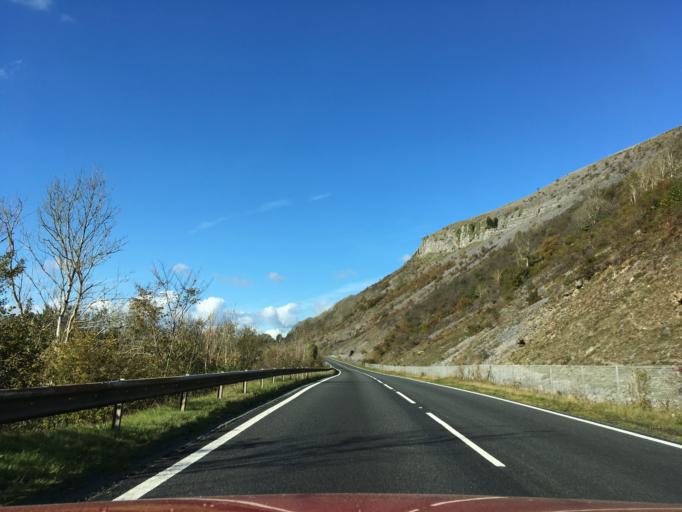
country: GB
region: Wales
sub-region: Merthyr Tydfil County Borough
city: Merthyr Tydfil
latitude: 51.7758
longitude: -3.4193
